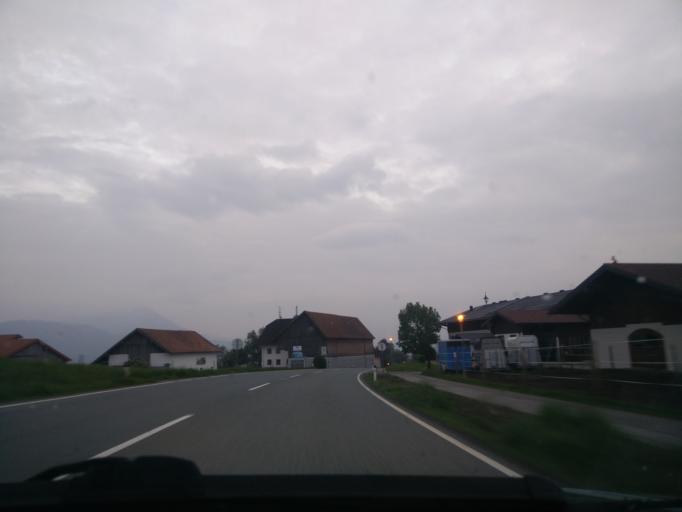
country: AT
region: Salzburg
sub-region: Politischer Bezirk Salzburg-Umgebung
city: Elixhausen
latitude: 47.8765
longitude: 13.0663
